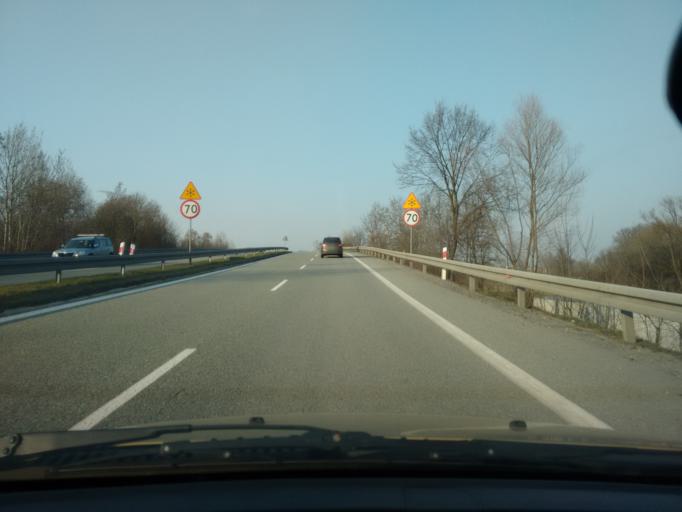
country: PL
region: Silesian Voivodeship
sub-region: Powiat cieszynski
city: Drogomysl
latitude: 49.8835
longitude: 18.7458
